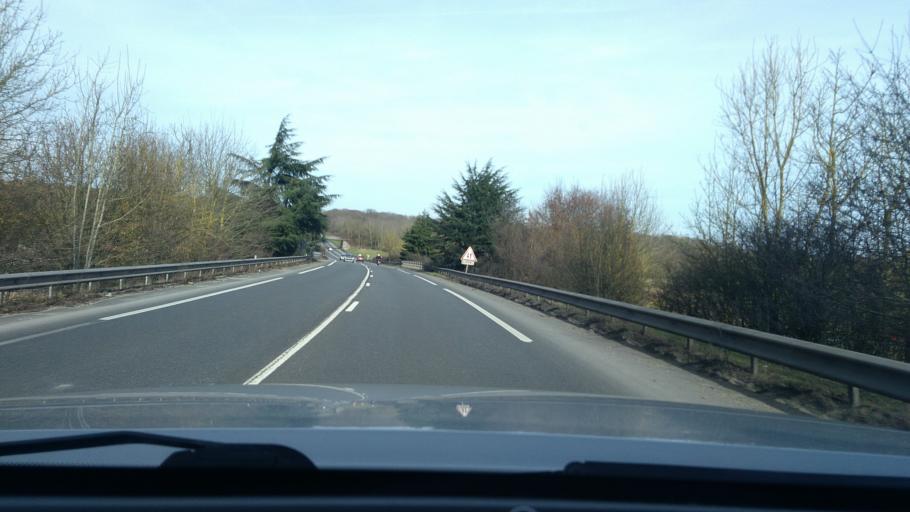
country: FR
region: Ile-de-France
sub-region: Departement de Seine-et-Marne
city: Guignes
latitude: 48.6379
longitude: 2.7913
